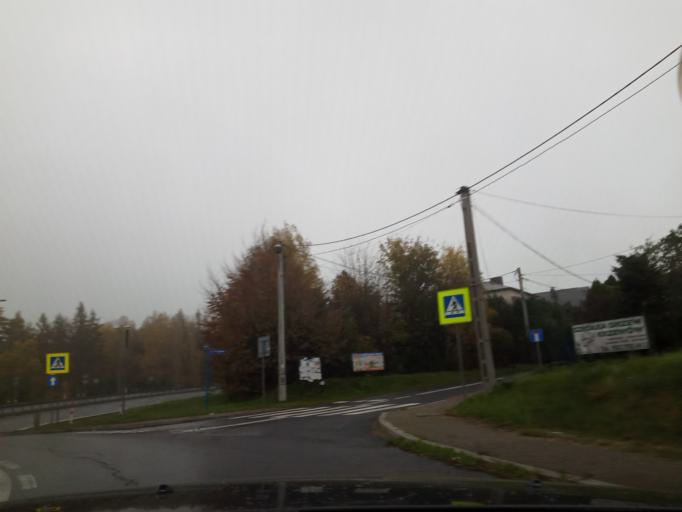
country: PL
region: Lesser Poland Voivodeship
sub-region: Powiat wielicki
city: Kokotow
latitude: 50.1145
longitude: 20.0866
